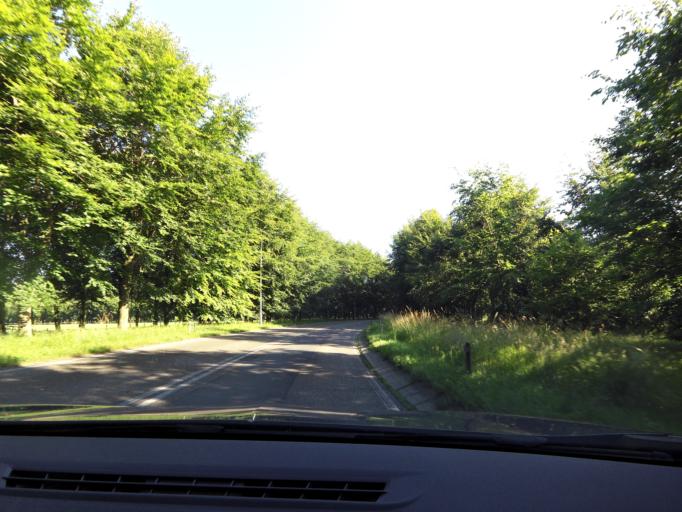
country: NL
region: Gelderland
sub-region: Gemeente Voorst
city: Twello
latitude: 52.2206
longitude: 6.1121
